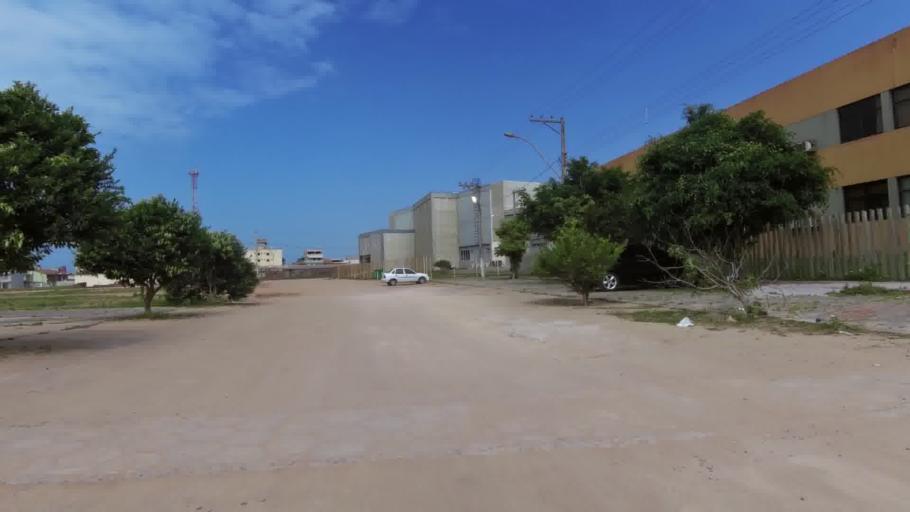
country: BR
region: Espirito Santo
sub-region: Itapemirim
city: Itapemirim
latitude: -21.0226
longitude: -40.8151
